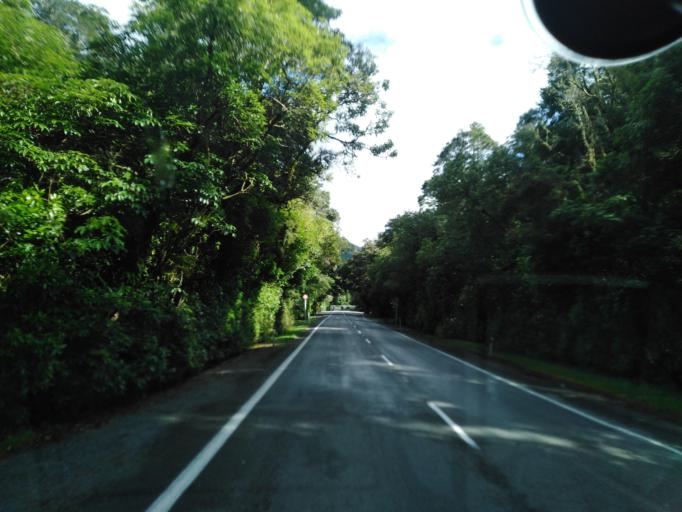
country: NZ
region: Nelson
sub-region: Nelson City
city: Nelson
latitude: -41.3006
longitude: 173.5735
